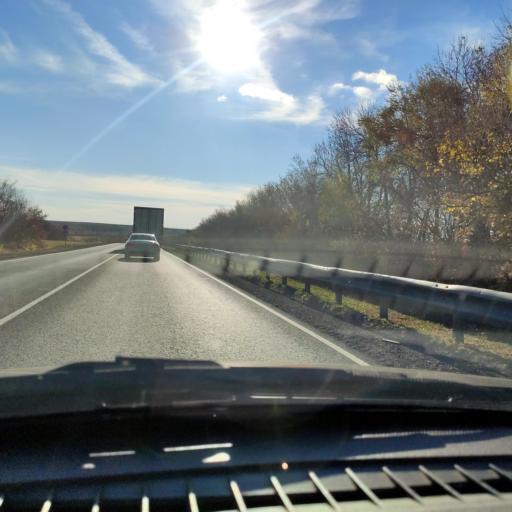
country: RU
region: Samara
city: Zhigulevsk
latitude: 53.3085
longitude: 49.3532
